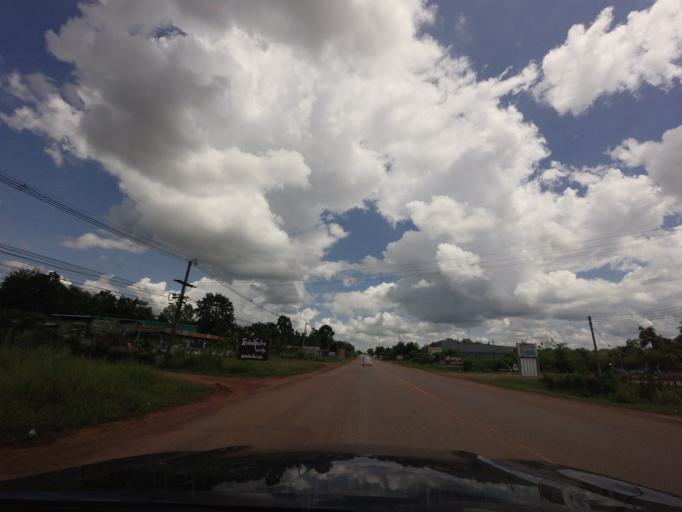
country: TH
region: Changwat Udon Thani
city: Ban Dung
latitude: 17.6779
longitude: 103.2446
